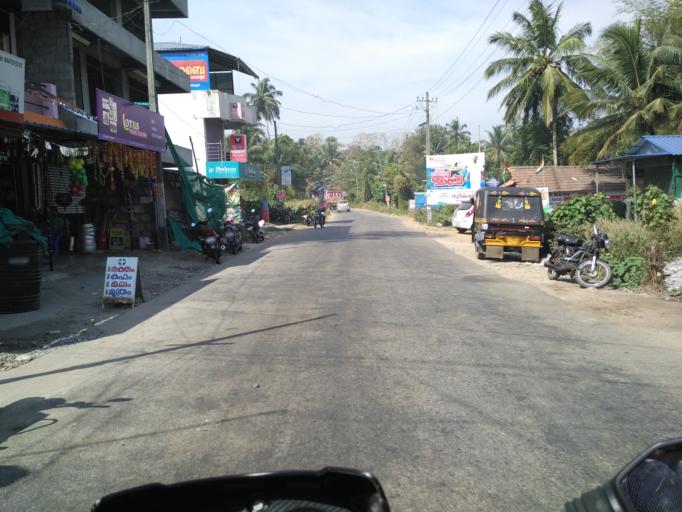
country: IN
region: Kerala
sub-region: Palakkad district
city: Palakkad
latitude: 10.6367
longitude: 76.5964
